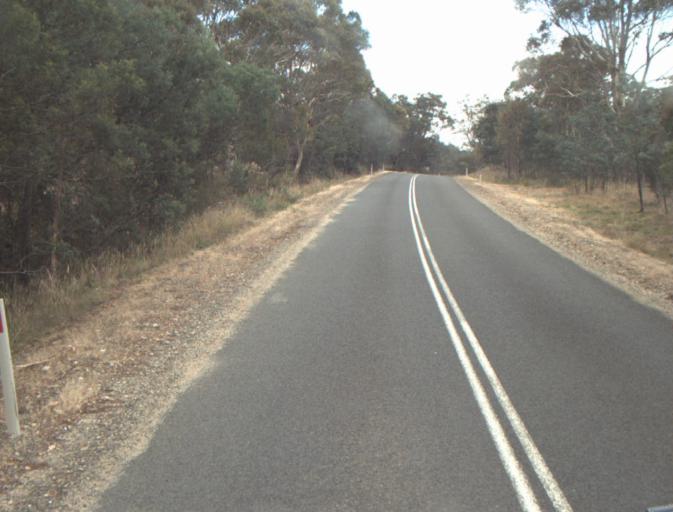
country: AU
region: Tasmania
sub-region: Northern Midlands
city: Evandale
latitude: -41.4993
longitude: 147.3838
